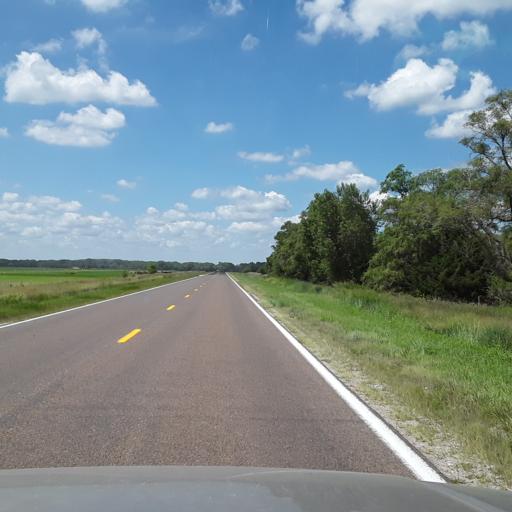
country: US
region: Nebraska
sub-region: Nance County
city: Genoa
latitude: 41.4040
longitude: -97.7069
